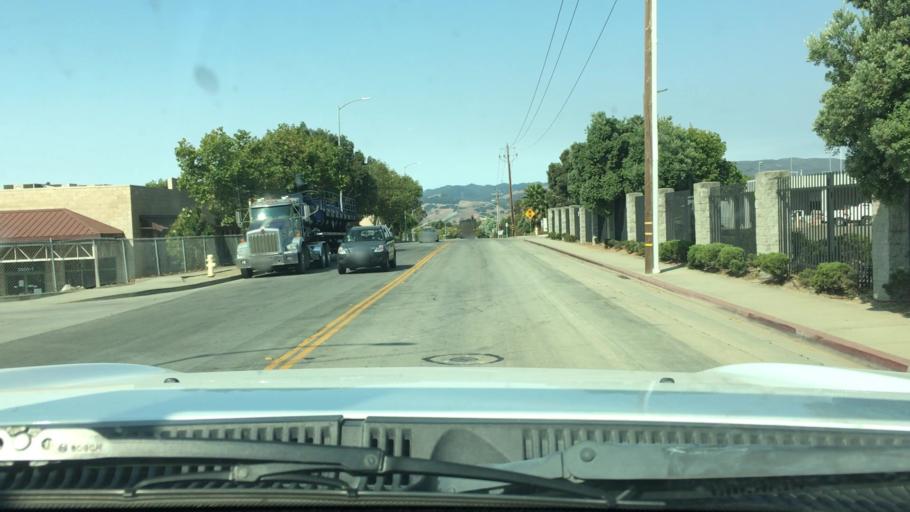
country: US
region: California
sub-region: San Luis Obispo County
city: San Luis Obispo
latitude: 35.2520
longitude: -120.6424
